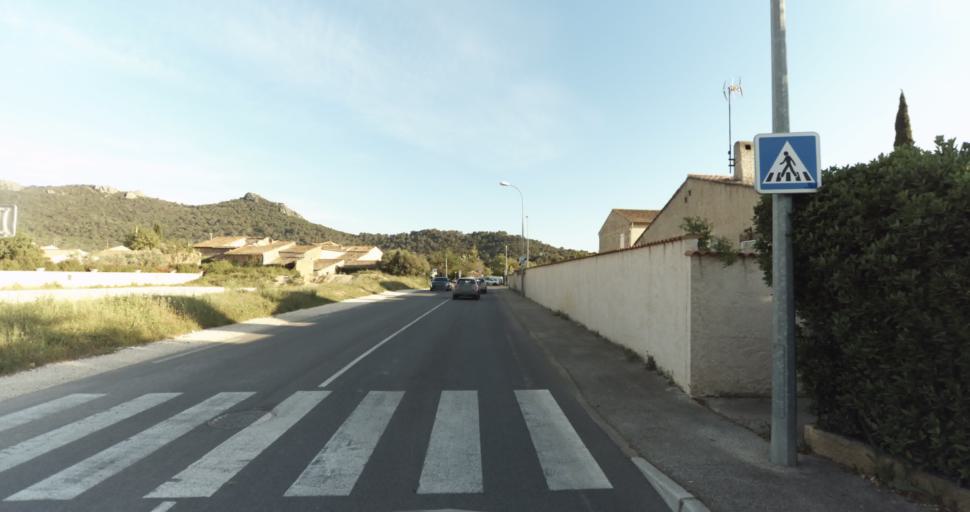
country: FR
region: Provence-Alpes-Cote d'Azur
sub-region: Departement du Var
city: La Crau
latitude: 43.1470
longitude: 6.0854
